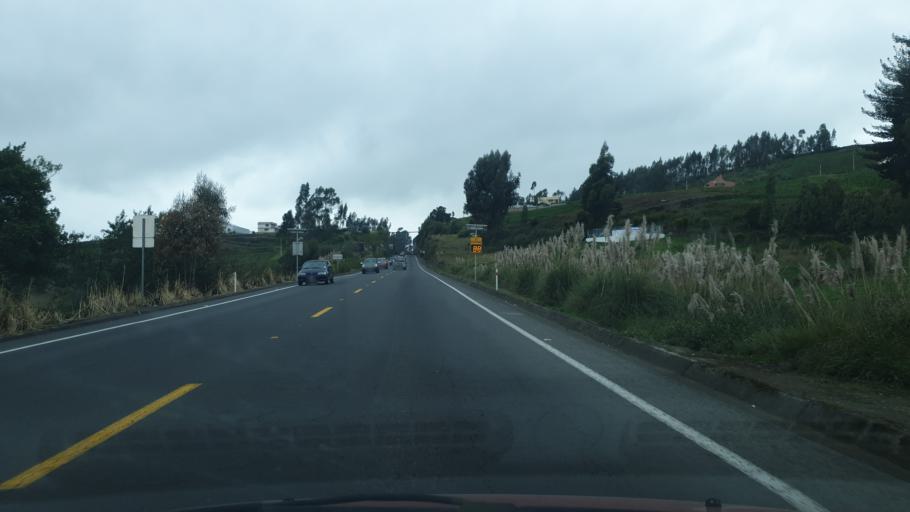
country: EC
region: Tungurahua
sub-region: Canton Quero
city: Quero
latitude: -1.3730
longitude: -78.6514
